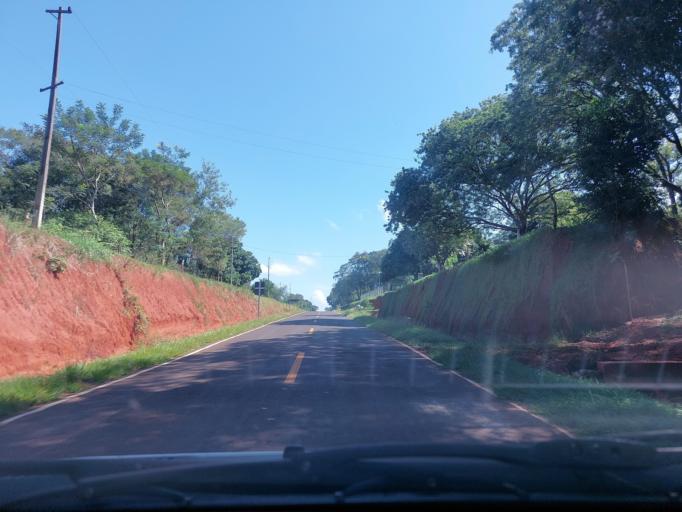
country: PY
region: San Pedro
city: Guayaybi
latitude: -24.5317
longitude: -56.5357
